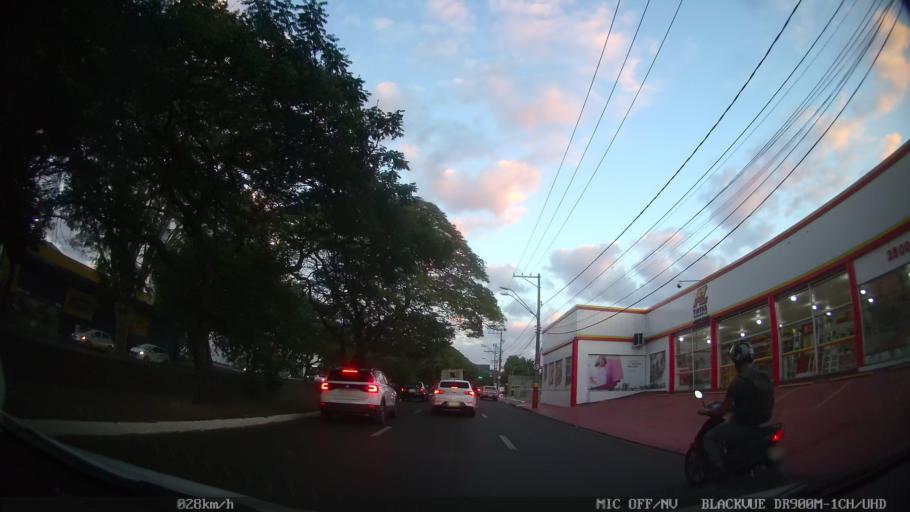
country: BR
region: Sao Paulo
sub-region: Ribeirao Preto
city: Ribeirao Preto
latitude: -21.1869
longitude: -47.7987
